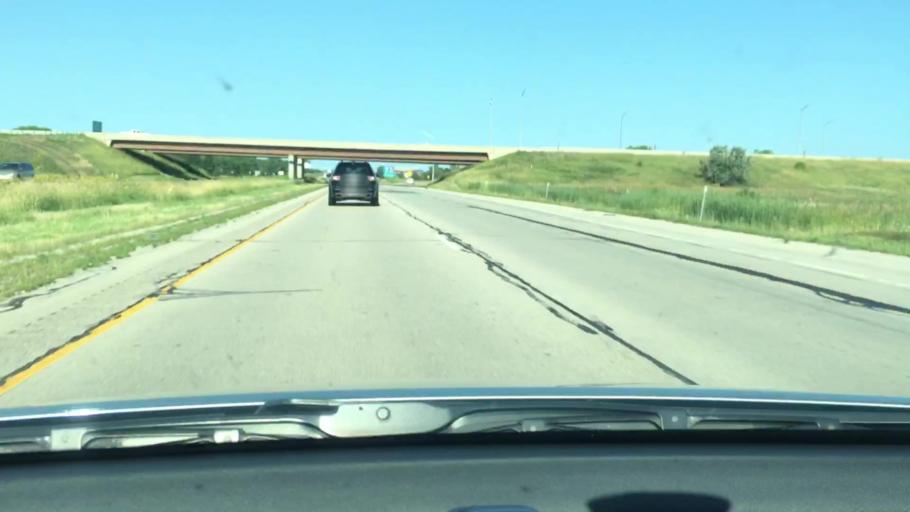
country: US
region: Wisconsin
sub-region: Outagamie County
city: Kimberly
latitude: 44.2982
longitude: -88.3538
